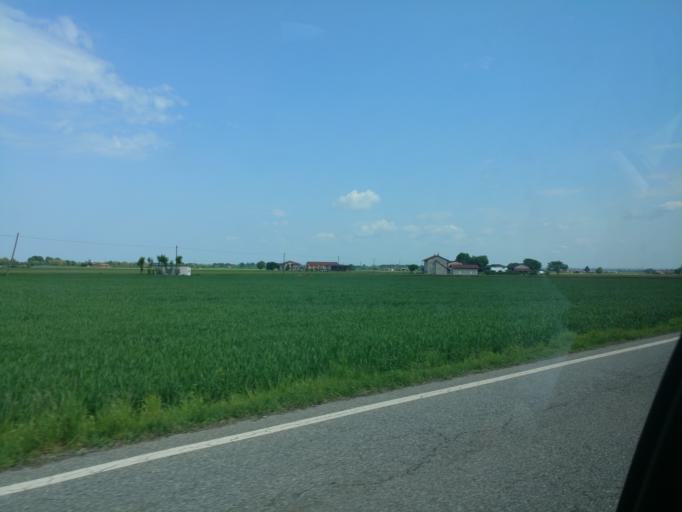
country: IT
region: Piedmont
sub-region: Provincia di Torino
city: Cavour
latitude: 44.7718
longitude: 7.3905
